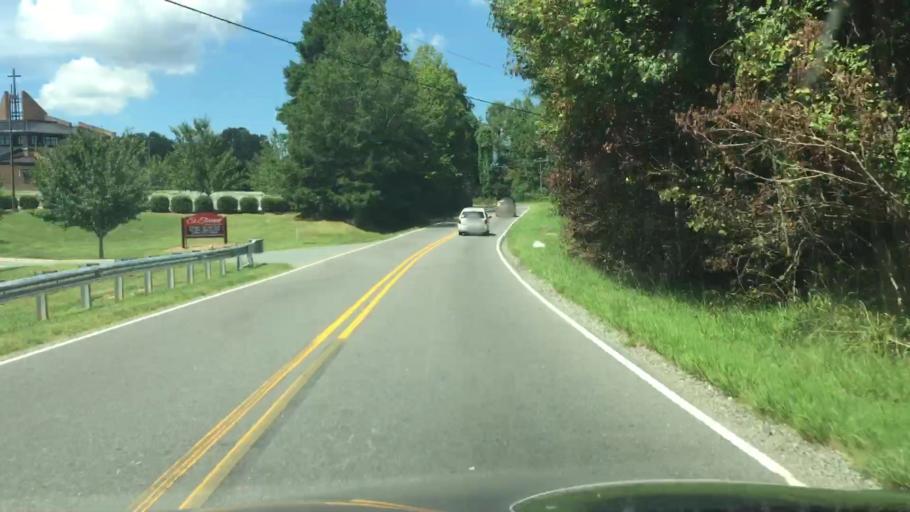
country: US
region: North Carolina
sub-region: Iredell County
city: Mooresville
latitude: 35.5771
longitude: -80.8449
